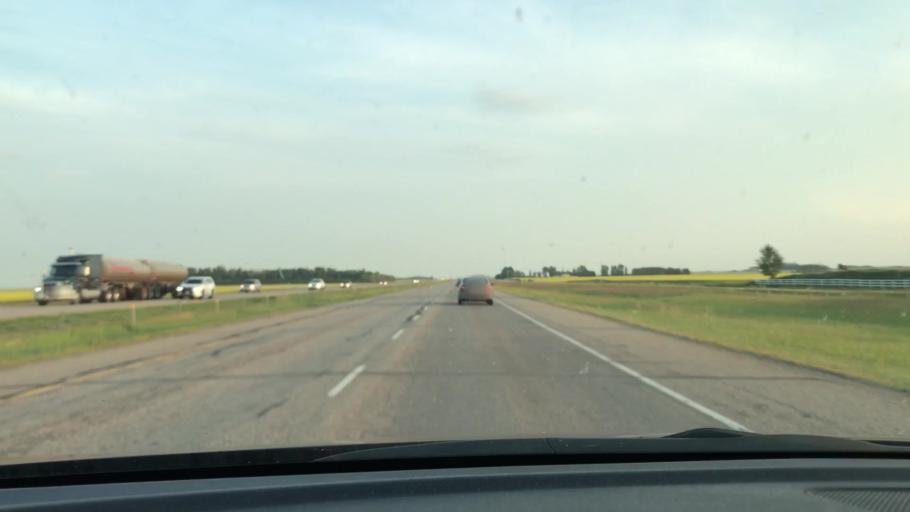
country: CA
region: Alberta
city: Olds
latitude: 51.8429
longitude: -114.0256
